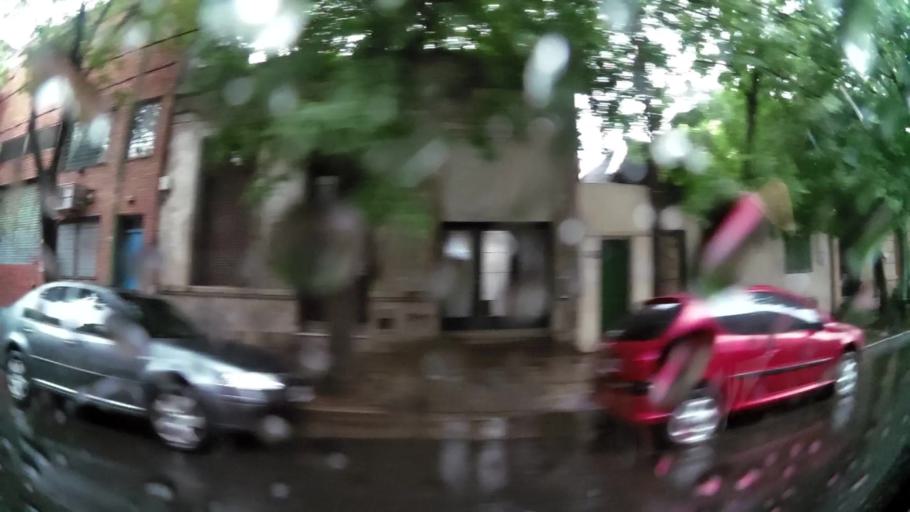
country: AR
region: Buenos Aires F.D.
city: Buenos Aires
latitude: -34.6323
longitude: -58.3558
